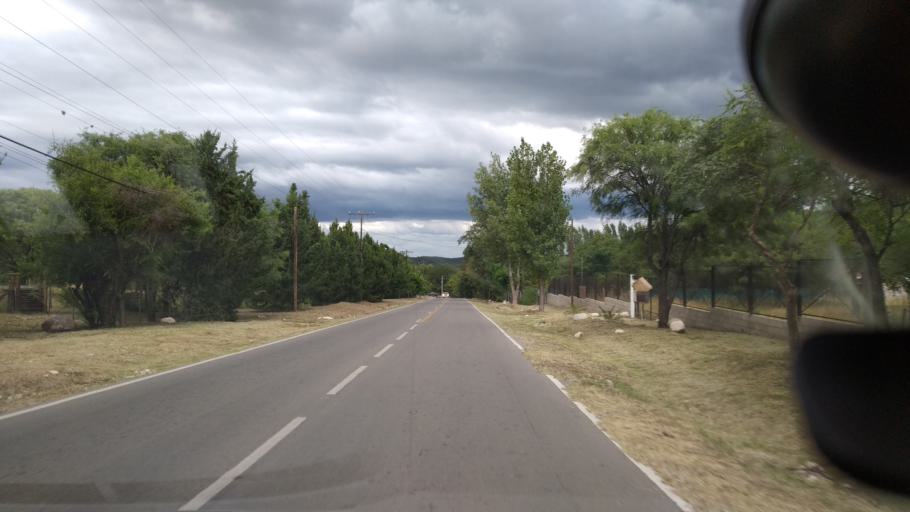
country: AR
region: Cordoba
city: Villa Las Rosas
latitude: -31.9378
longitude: -65.0385
